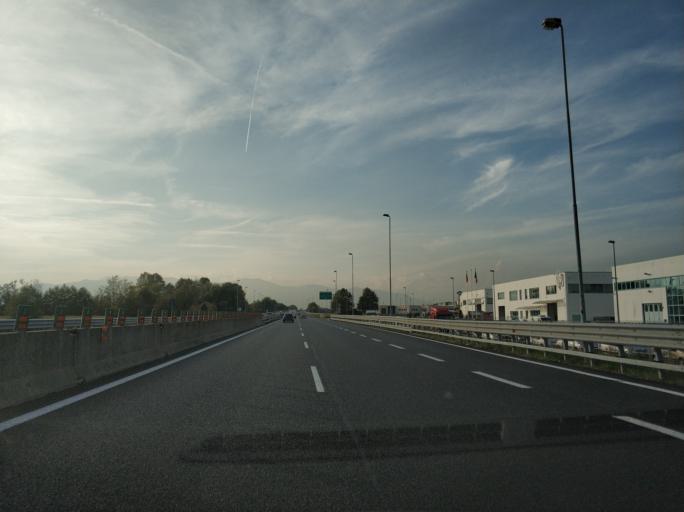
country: IT
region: Piedmont
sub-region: Provincia di Torino
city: Caselle Torinese
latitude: 45.1768
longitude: 7.6609
